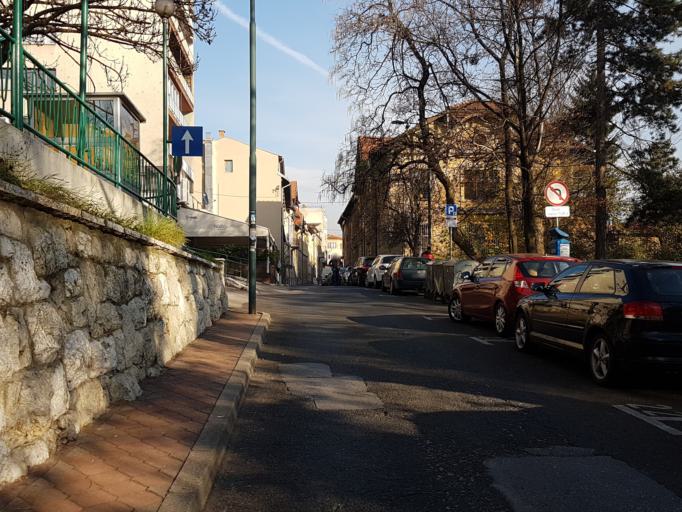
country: BA
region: Federation of Bosnia and Herzegovina
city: Kobilja Glava
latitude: 43.8610
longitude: 18.4170
